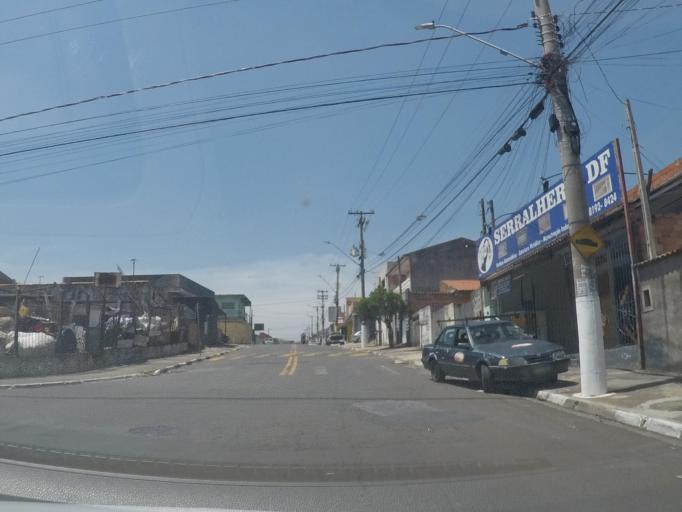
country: BR
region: Sao Paulo
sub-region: Hortolandia
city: Hortolandia
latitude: -22.8567
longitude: -47.2061
